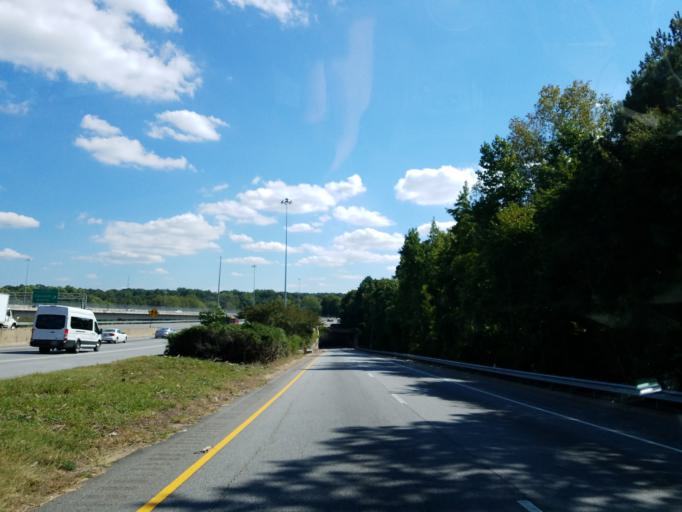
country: US
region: Georgia
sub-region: Fulton County
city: Hapeville
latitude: 33.6905
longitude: -84.4023
